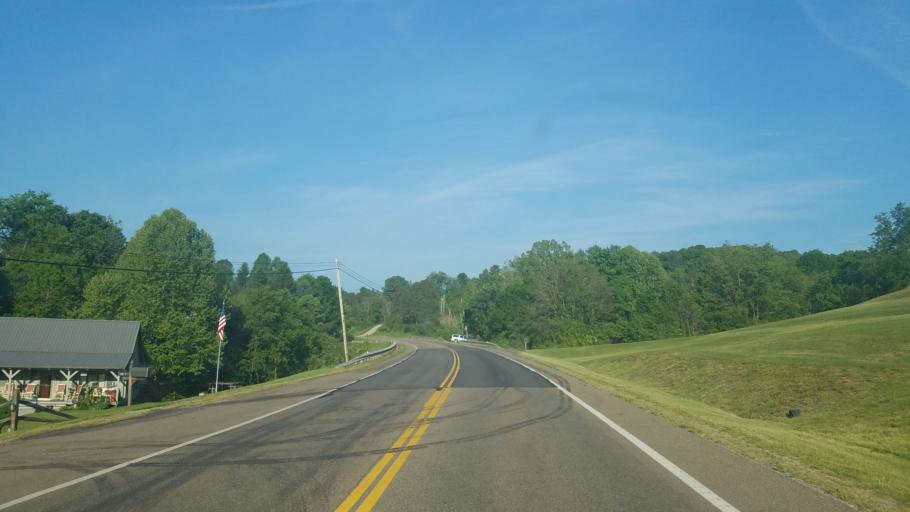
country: US
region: West Virginia
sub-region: Mason County
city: New Haven
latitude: 39.1176
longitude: -81.9086
